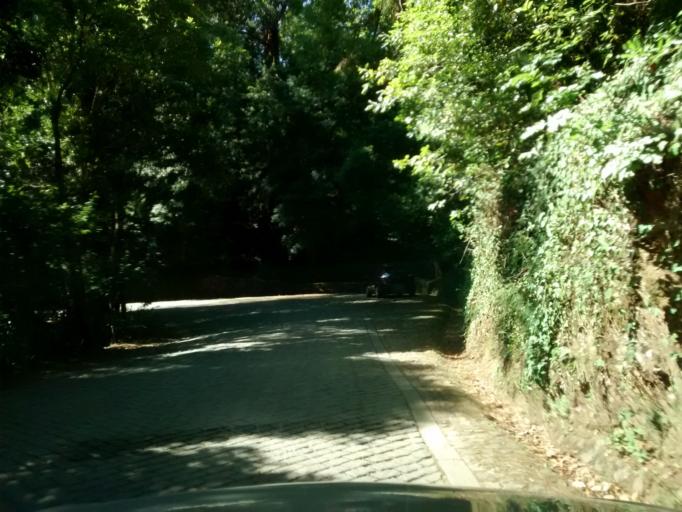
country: PT
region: Aveiro
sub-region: Mealhada
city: Pampilhosa do Botao
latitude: 40.3790
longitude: -8.3695
